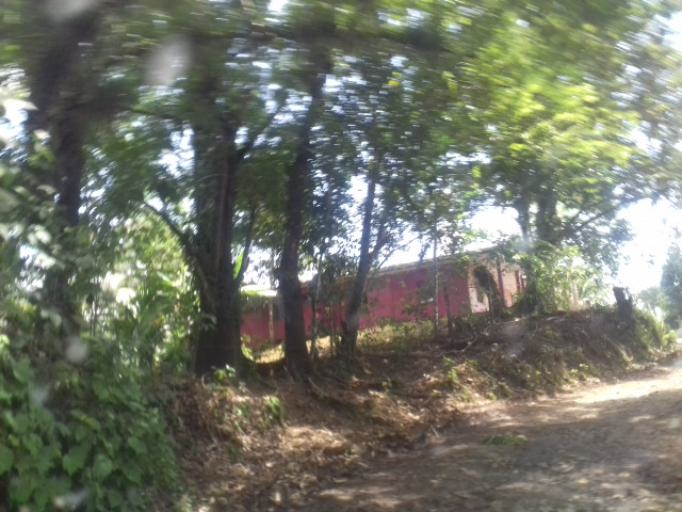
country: NI
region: Matagalpa
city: Rio Blanco
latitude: 12.9725
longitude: -85.3701
